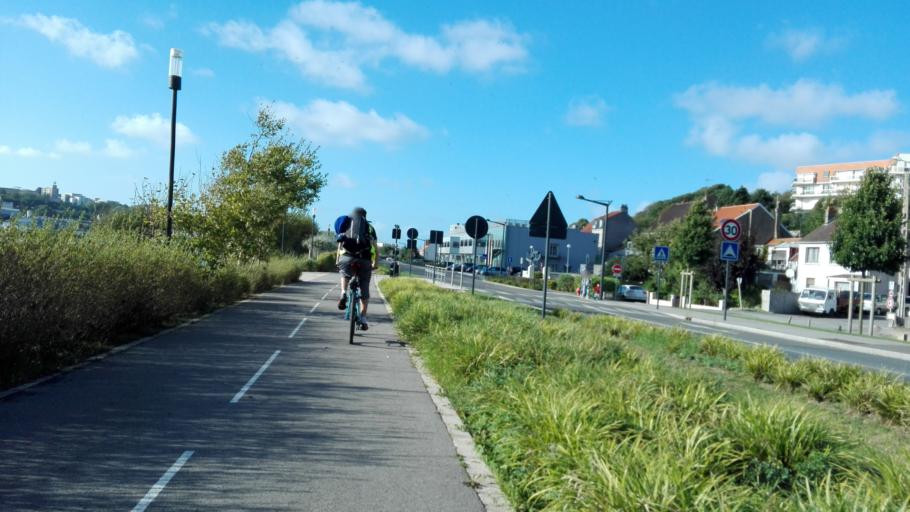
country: FR
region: Nord-Pas-de-Calais
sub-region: Departement du Pas-de-Calais
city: Boulogne-sur-Mer
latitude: 50.7061
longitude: 1.6129
